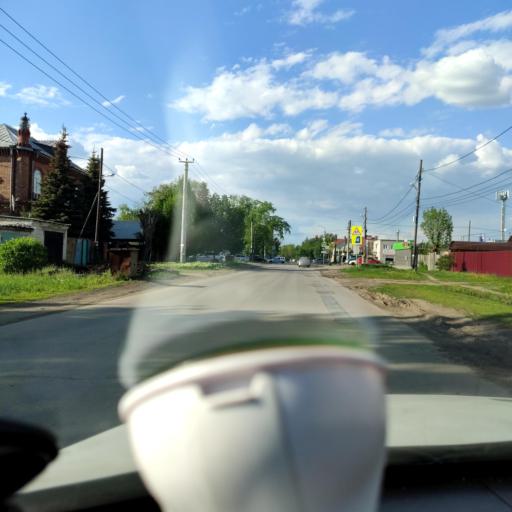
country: RU
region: Samara
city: Petra-Dubrava
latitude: 53.2511
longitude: 50.3383
